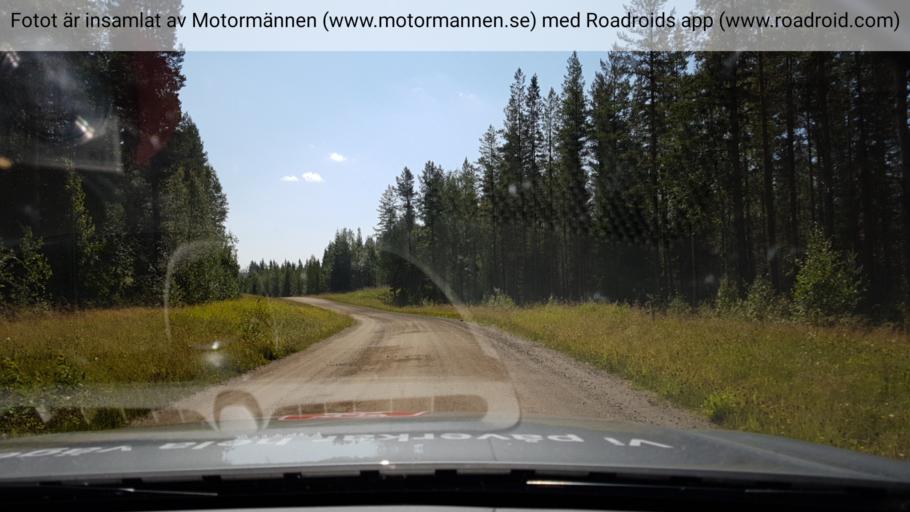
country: SE
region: Jaemtland
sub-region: Stroemsunds Kommun
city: Stroemsund
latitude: 63.3241
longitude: 15.4688
